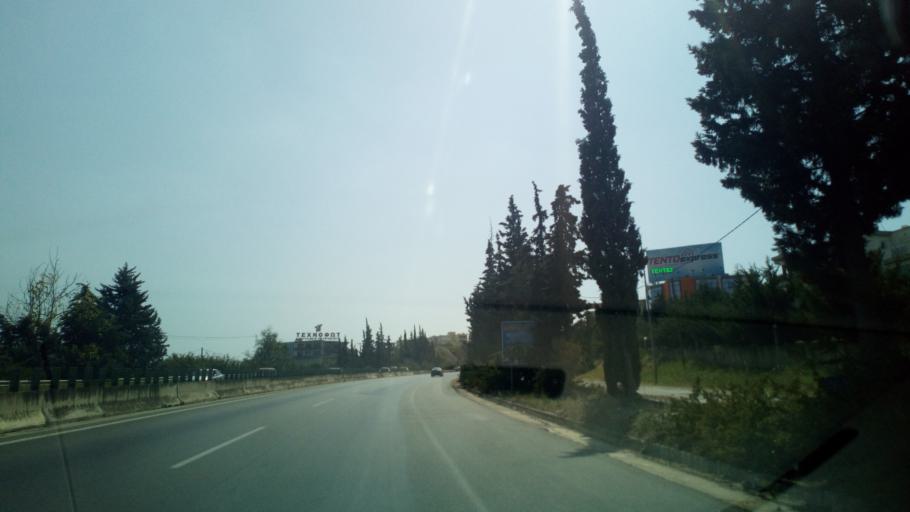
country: GR
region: Central Macedonia
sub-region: Nomos Thessalonikis
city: Neo Rysi
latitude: 40.4884
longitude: 22.9978
